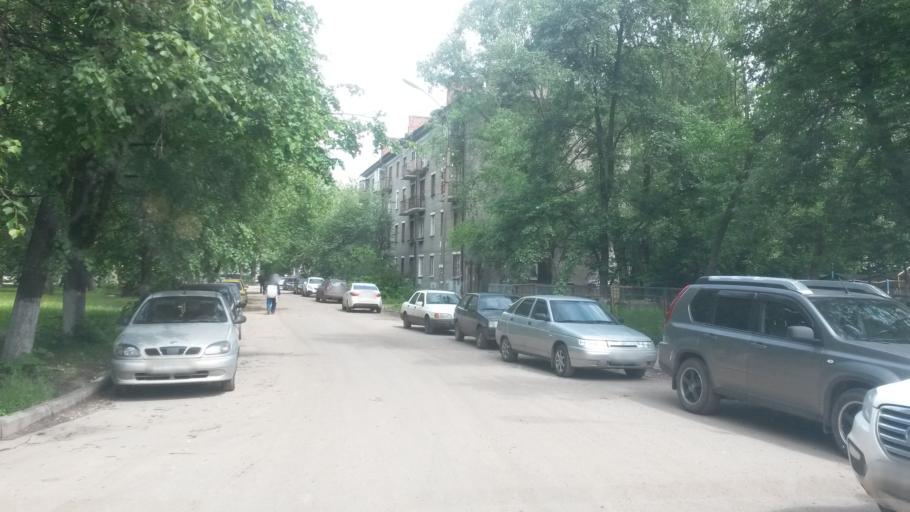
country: RU
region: Jaroslavl
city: Yaroslavl
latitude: 57.6413
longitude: 39.8719
